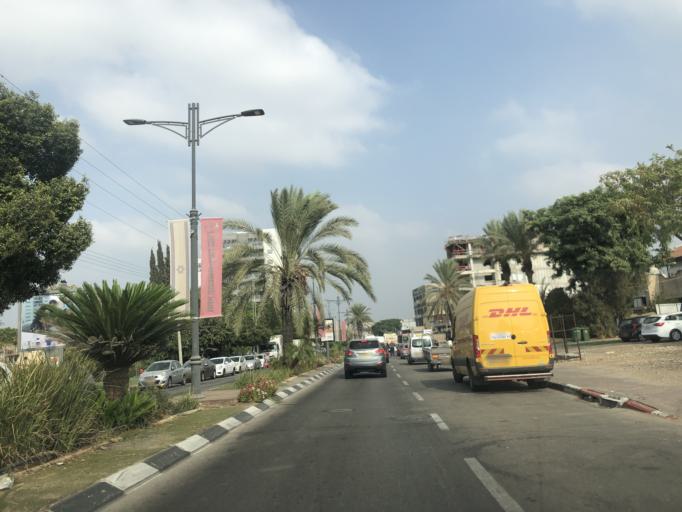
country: IL
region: Central District
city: Rosh Ha'Ayin
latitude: 32.0941
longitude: 34.9425
